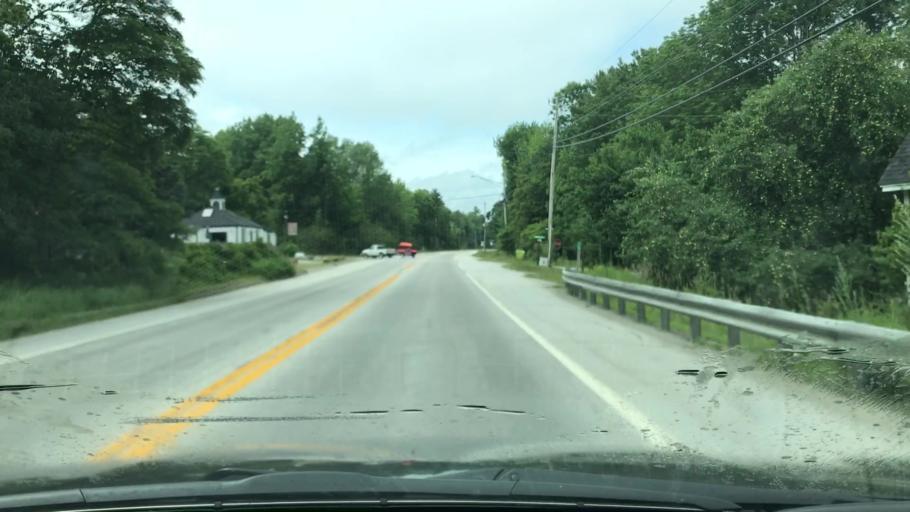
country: US
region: Maine
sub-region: Waldo County
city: Northport
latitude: 44.3373
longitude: -68.9608
